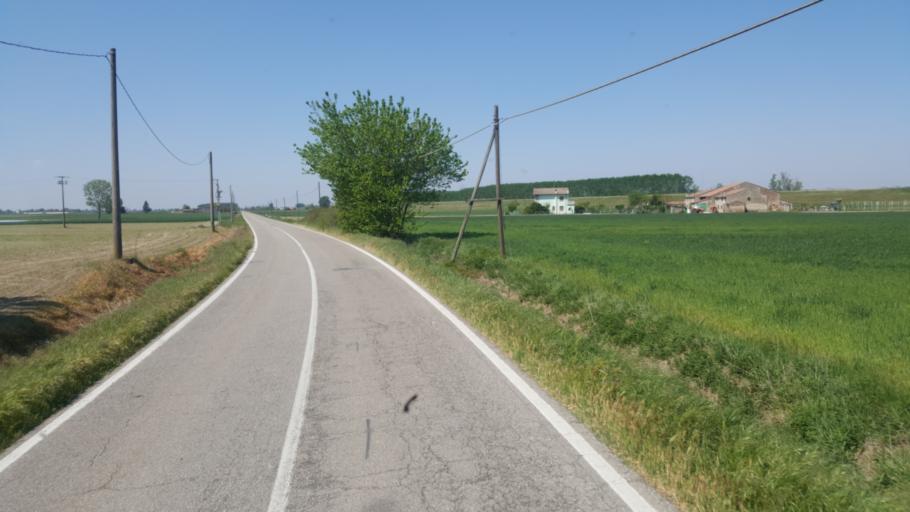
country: IT
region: Veneto
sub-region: Provincia di Rovigo
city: Salara
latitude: 44.9642
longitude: 11.4095
